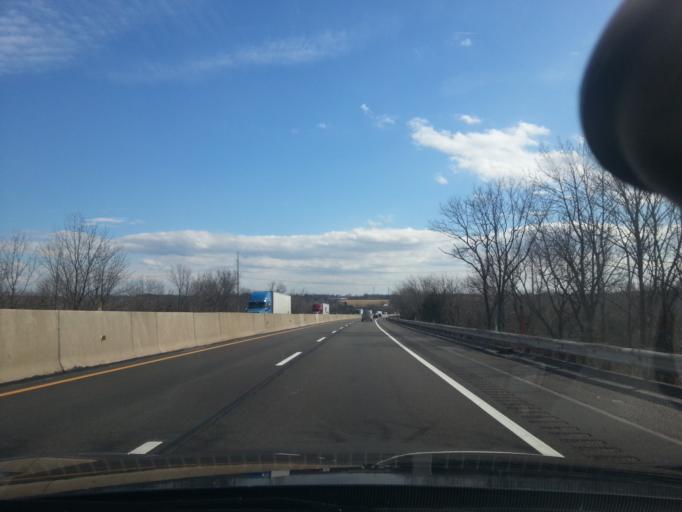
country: US
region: Pennsylvania
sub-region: Montgomery County
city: Telford
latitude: 40.3376
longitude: -75.3838
